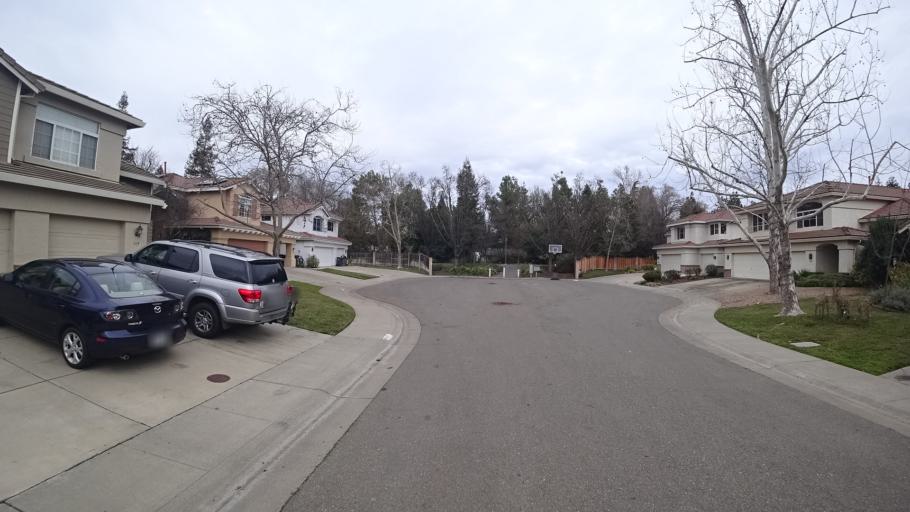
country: US
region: California
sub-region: Yolo County
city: Davis
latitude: 38.5561
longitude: -121.7158
